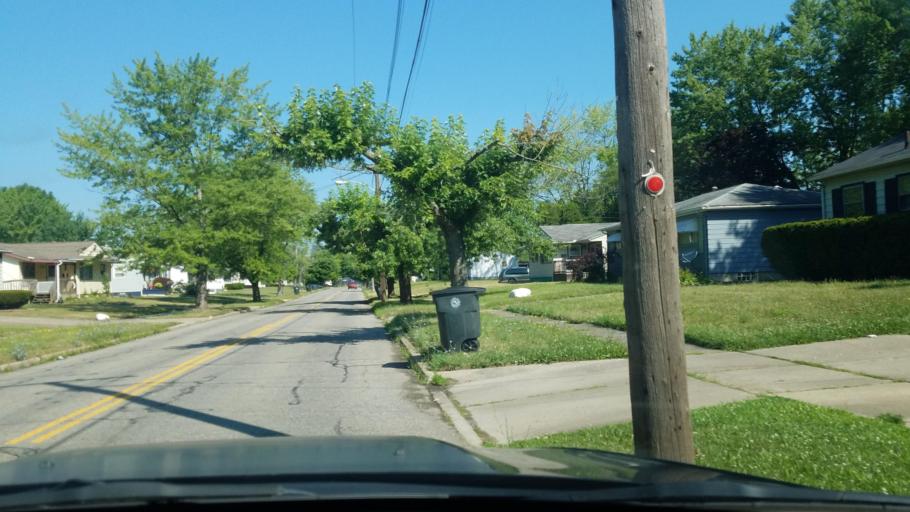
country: US
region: Ohio
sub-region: Trumbull County
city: Leavittsburg
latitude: 41.2483
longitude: -80.8564
